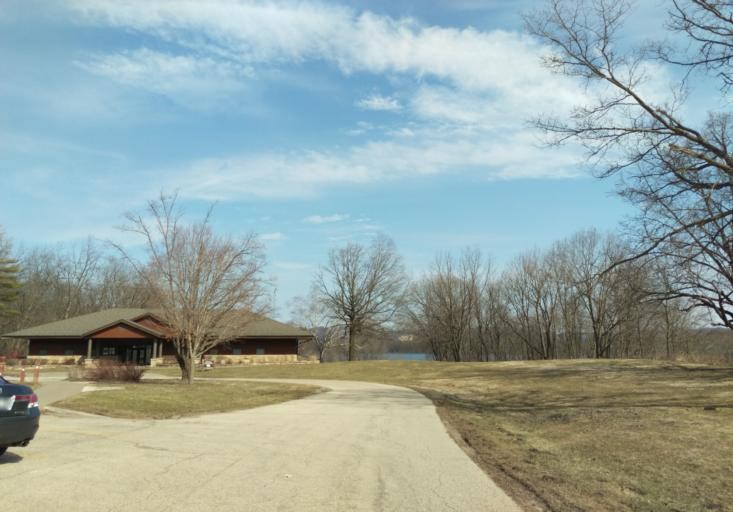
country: US
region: Wisconsin
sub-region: Crawford County
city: Prairie du Chien
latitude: 43.0885
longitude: -91.1866
